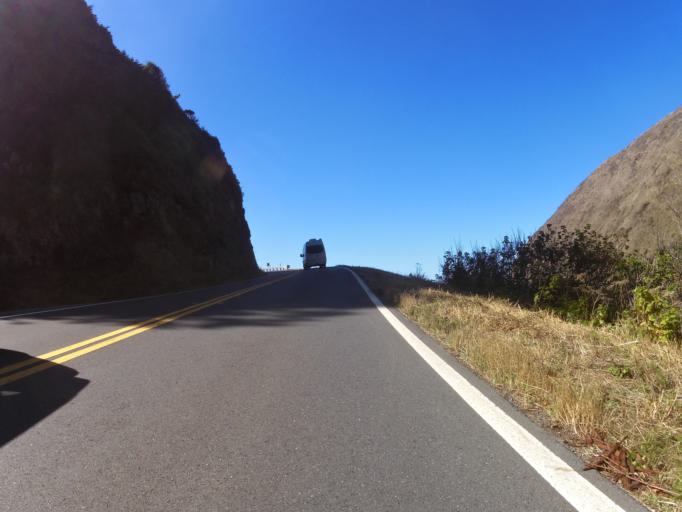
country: US
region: California
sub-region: Mendocino County
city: Fort Bragg
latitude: 39.6131
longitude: -123.7792
